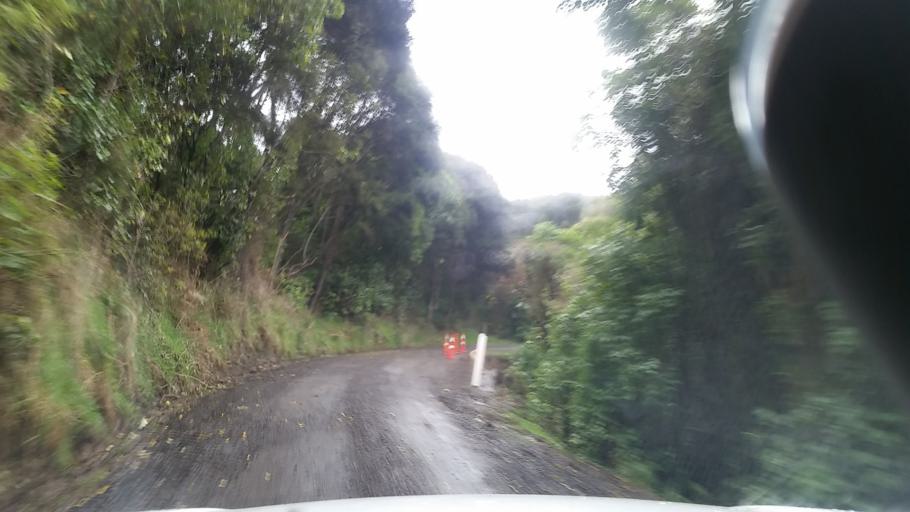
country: NZ
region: Canterbury
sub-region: Christchurch City
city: Christchurch
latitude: -43.7579
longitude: 173.0494
